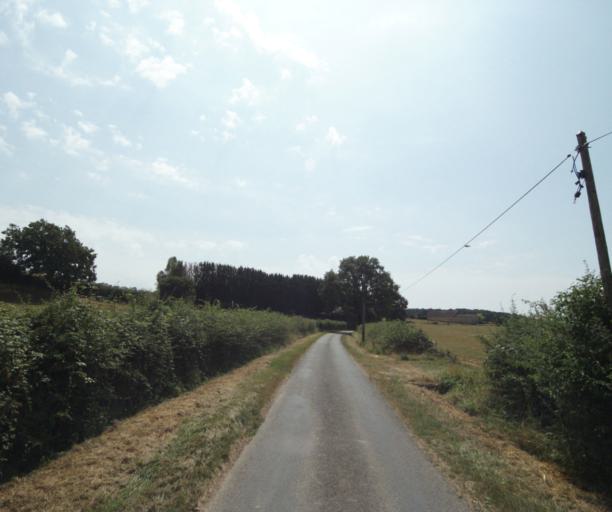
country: FR
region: Bourgogne
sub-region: Departement de Saone-et-Loire
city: Gueugnon
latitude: 46.5679
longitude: 4.0598
